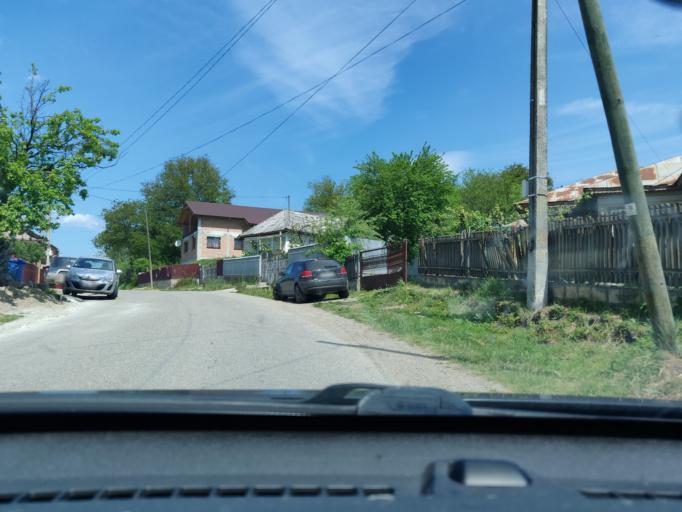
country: RO
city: Vizantea-Manastireasca
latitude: 45.9759
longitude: 26.8099
